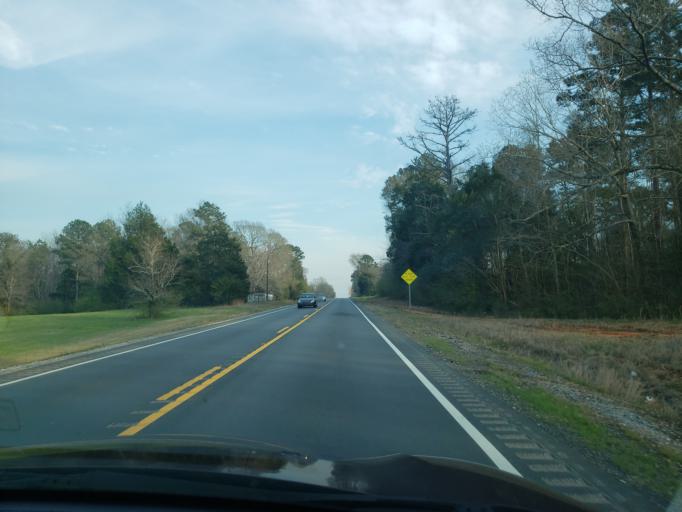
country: US
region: Alabama
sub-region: Hale County
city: Moundville
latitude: 32.8970
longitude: -87.6232
